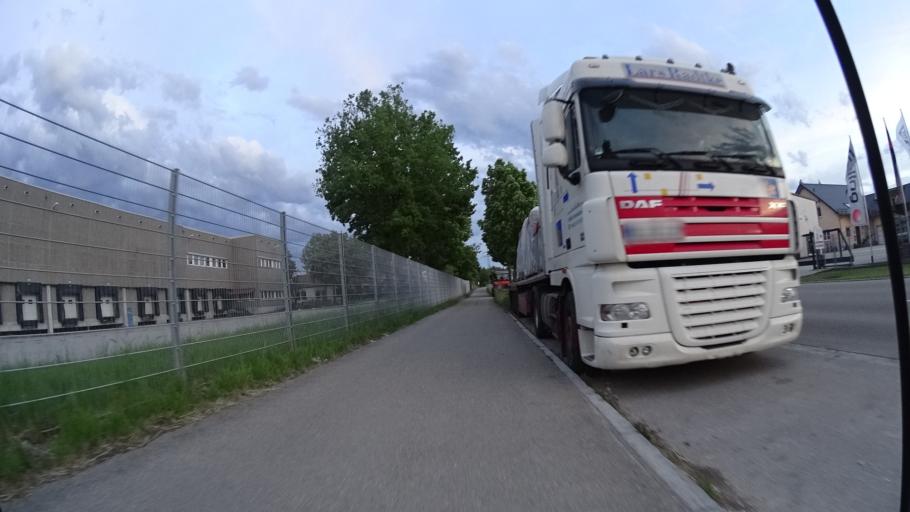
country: DE
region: Bavaria
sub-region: Swabia
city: Pfaffenhofen an der Roth
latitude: 48.3571
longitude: 10.1503
